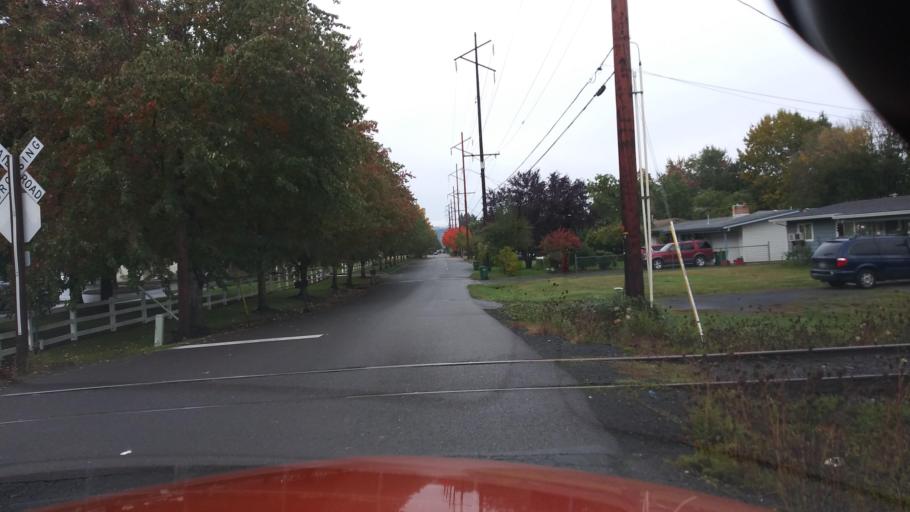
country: US
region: Oregon
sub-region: Washington County
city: Forest Grove
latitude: 45.5241
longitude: -123.0880
